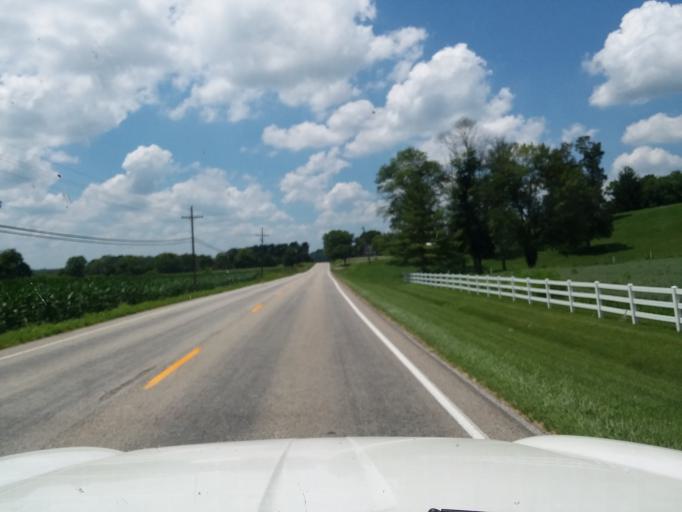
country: US
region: Indiana
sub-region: Johnson County
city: Trafalgar
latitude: 39.3717
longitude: -86.2869
